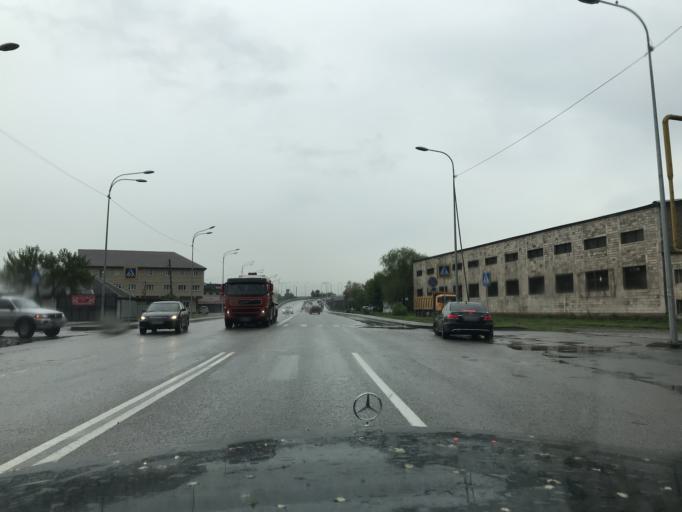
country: KZ
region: Almaty Oblysy
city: Pervomayskiy
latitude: 43.3417
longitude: 76.9666
